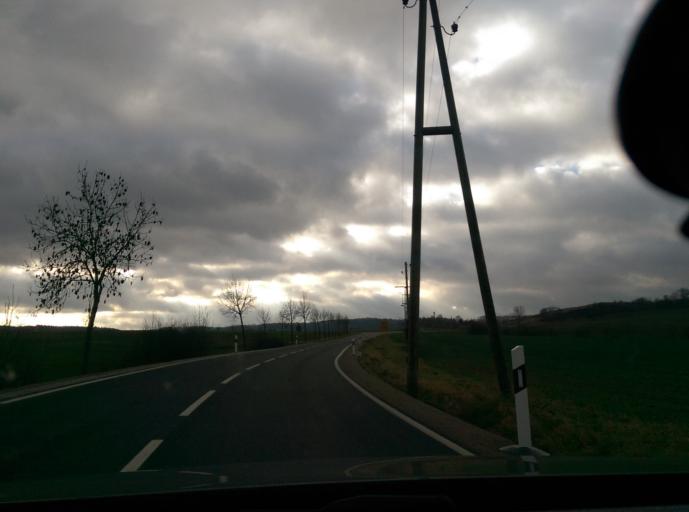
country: DE
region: Thuringia
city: Krauthausen
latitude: 51.0223
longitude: 10.2609
